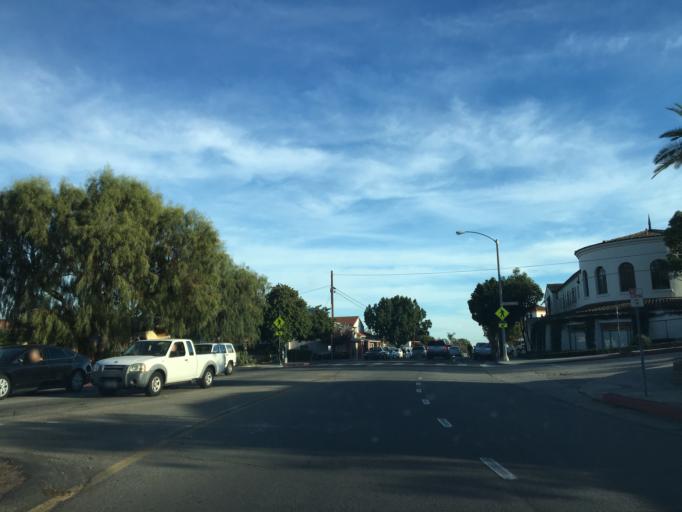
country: US
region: California
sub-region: Santa Barbara County
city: Mission Canyon
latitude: 34.4402
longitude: -119.7302
